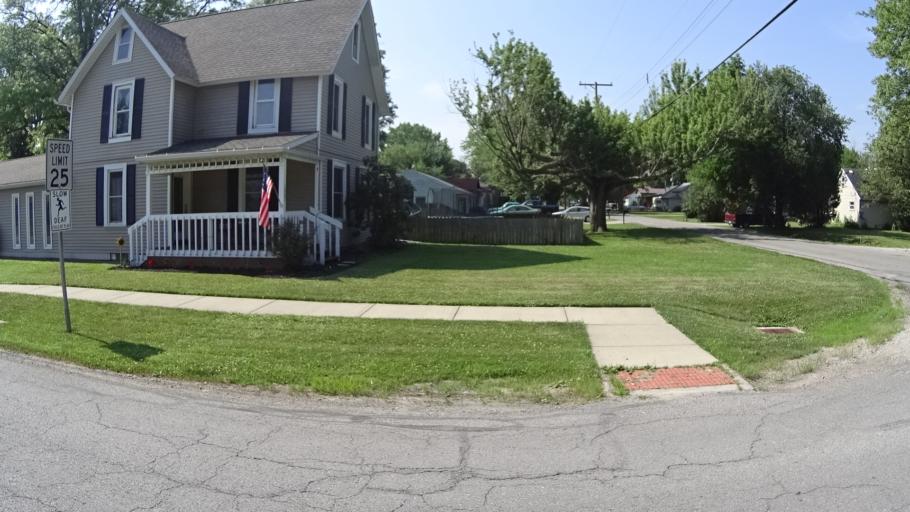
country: US
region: Ohio
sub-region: Lorain County
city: Vermilion
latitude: 41.4161
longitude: -82.3769
